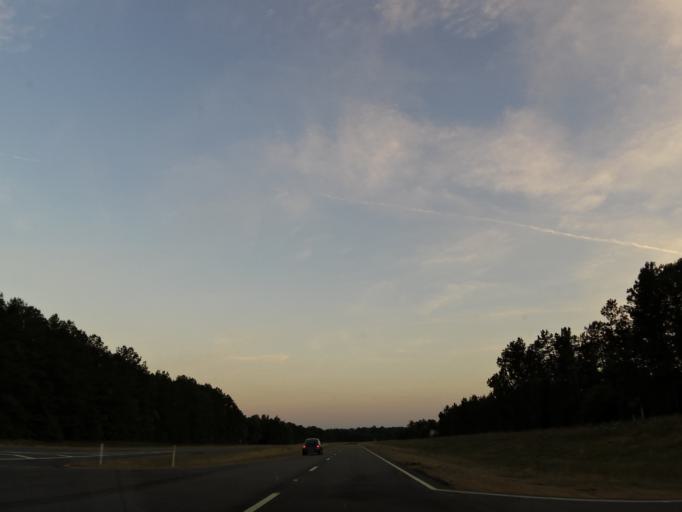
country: US
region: Mississippi
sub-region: Kemper County
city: De Kalb
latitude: 32.8121
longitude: -88.4565
